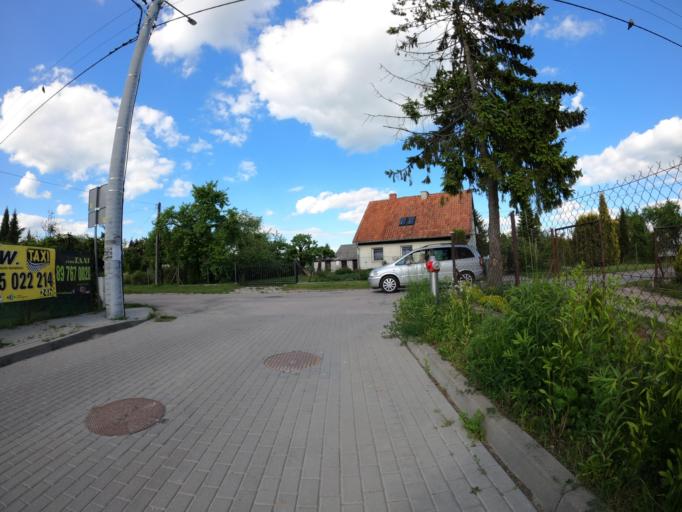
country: PL
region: Warmian-Masurian Voivodeship
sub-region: Powiat lidzbarski
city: Lidzbark Warminski
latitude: 54.1298
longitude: 20.5956
